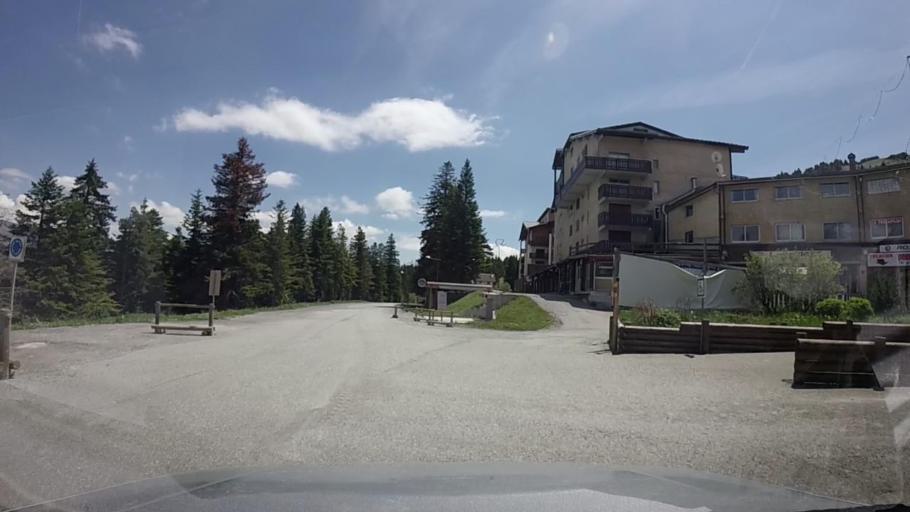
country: FR
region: Provence-Alpes-Cote d'Azur
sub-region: Departement des Alpes-de-Haute-Provence
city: Seyne-les-Alpes
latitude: 44.3476
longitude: 6.2937
